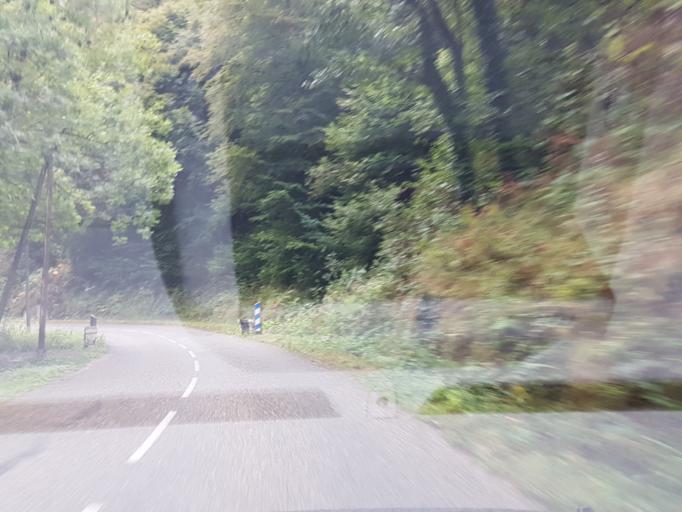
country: FR
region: Midi-Pyrenees
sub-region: Departement de l'Ariege
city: Saint-Girons
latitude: 42.9091
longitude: 1.2717
